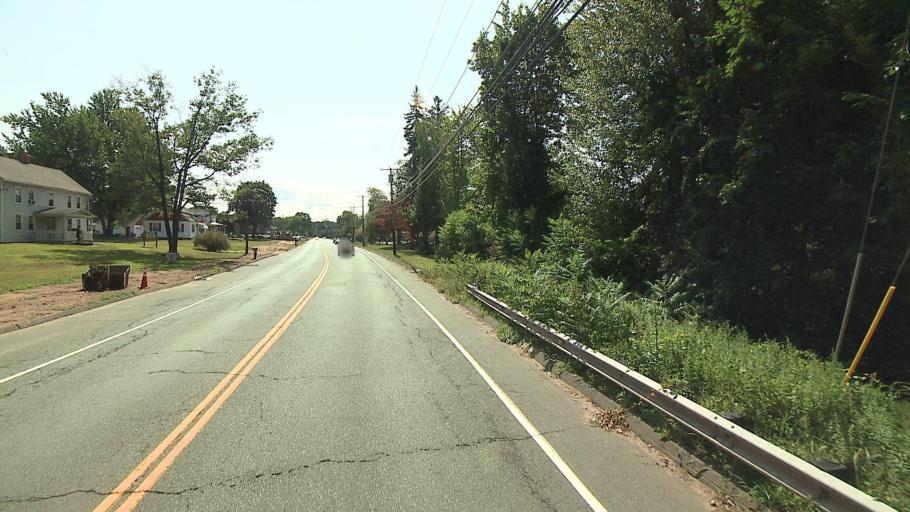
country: US
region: Connecticut
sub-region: Hartford County
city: Windsor Locks
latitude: 41.9031
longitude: -72.6121
